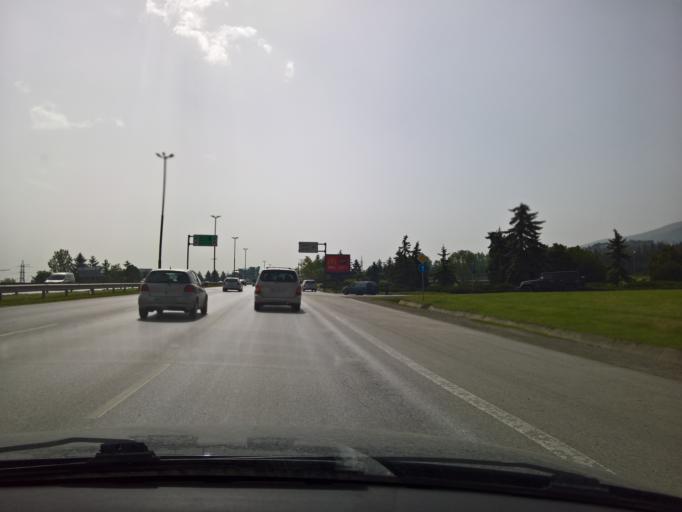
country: BG
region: Sofia-Capital
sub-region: Stolichna Obshtina
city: Sofia
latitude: 42.6538
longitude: 23.2824
